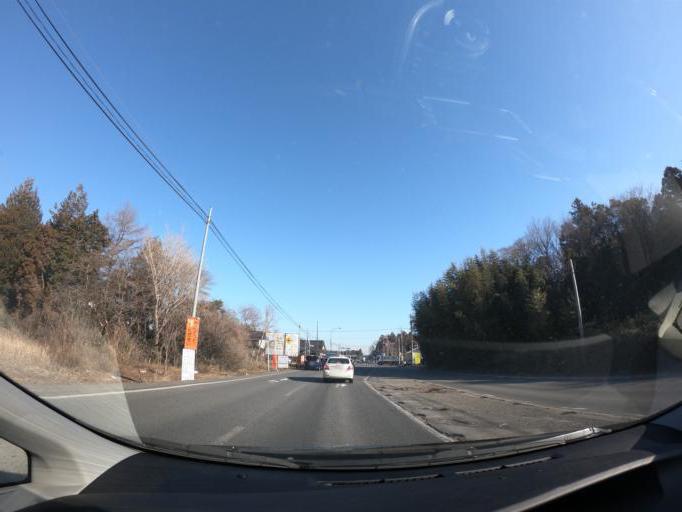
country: JP
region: Ibaraki
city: Ishige
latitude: 36.0954
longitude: 140.0357
